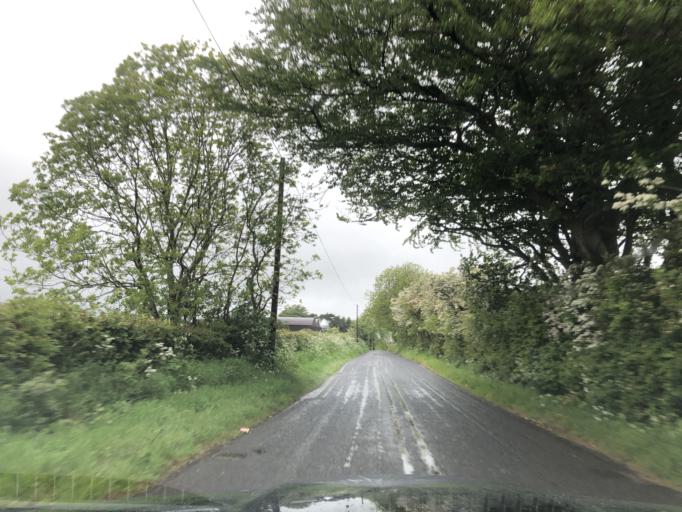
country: GB
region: Northern Ireland
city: Dunloy
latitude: 55.1120
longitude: -6.3460
